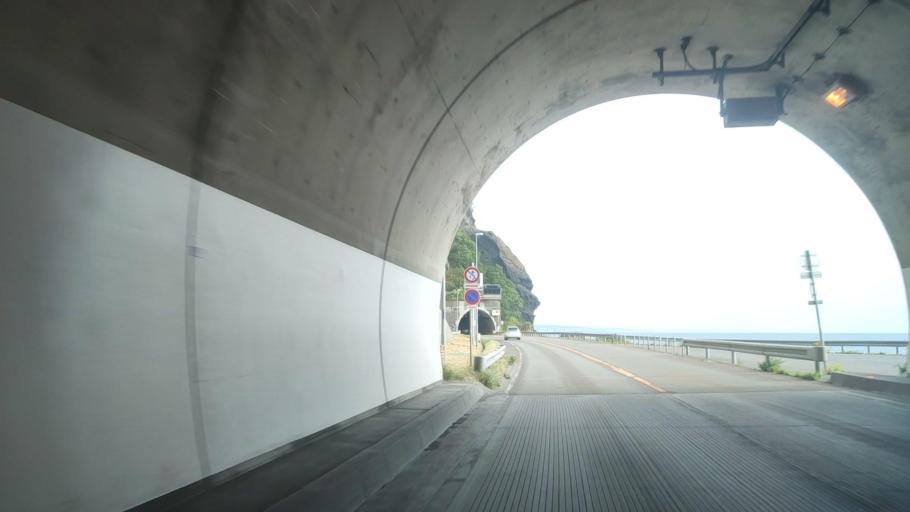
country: JP
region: Hokkaido
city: Ishikari
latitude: 43.4500
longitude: 141.4096
